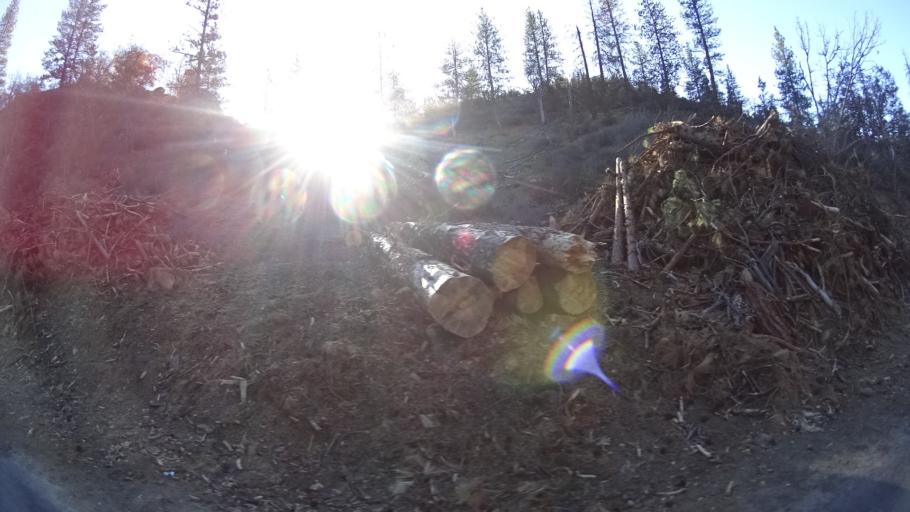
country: US
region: Oregon
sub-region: Jackson County
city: Ashland
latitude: 41.9814
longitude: -122.6247
